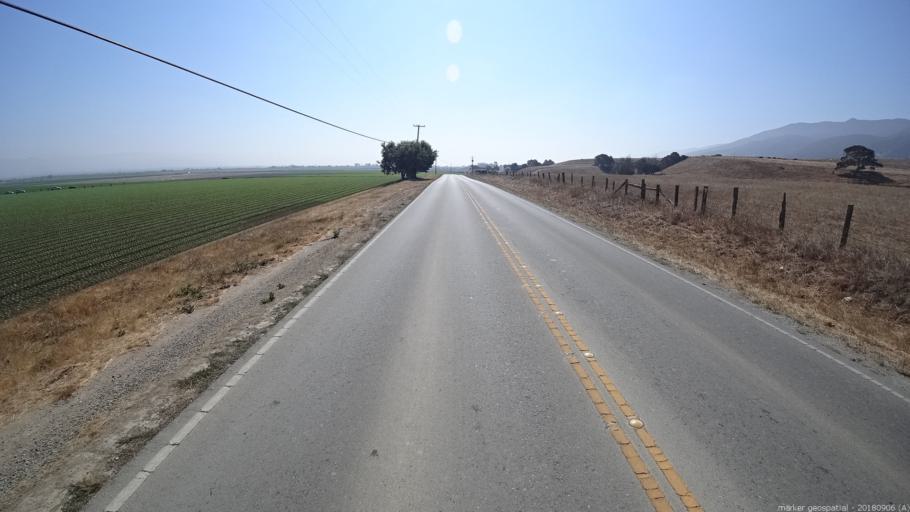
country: US
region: California
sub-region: Monterey County
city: Chualar
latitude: 36.5716
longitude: -121.5730
